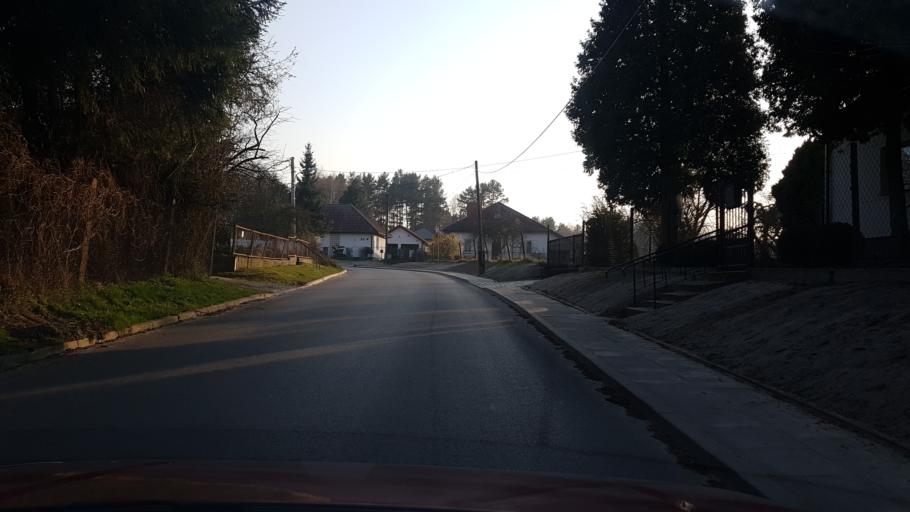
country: PL
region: West Pomeranian Voivodeship
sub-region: Powiat gryfinski
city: Stare Czarnowo
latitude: 53.3382
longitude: 14.7495
